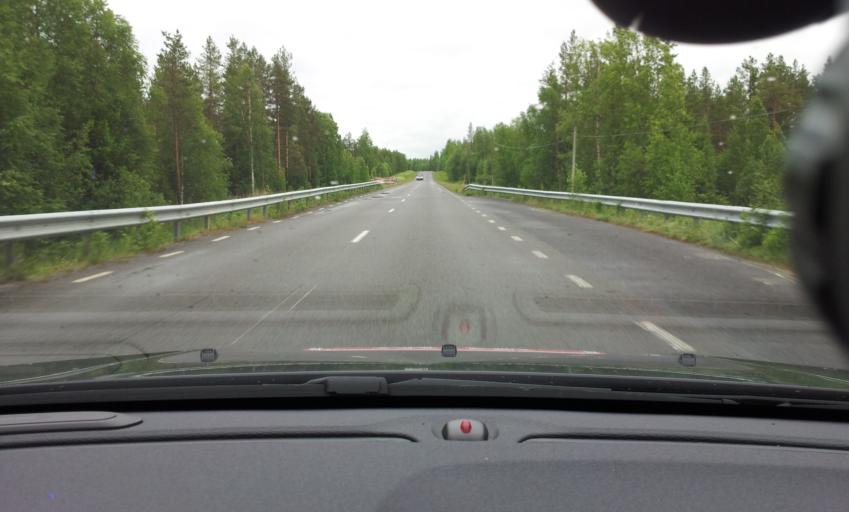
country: SE
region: Jaemtland
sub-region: OEstersunds Kommun
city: Lit
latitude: 63.7031
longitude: 14.9902
